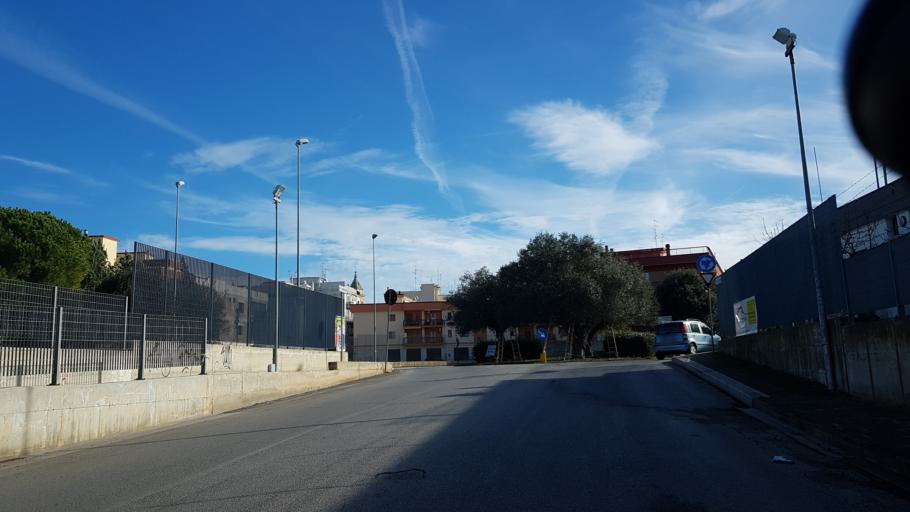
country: IT
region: Apulia
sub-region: Provincia di Bari
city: Gioia del Colle
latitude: 40.8005
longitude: 16.9174
